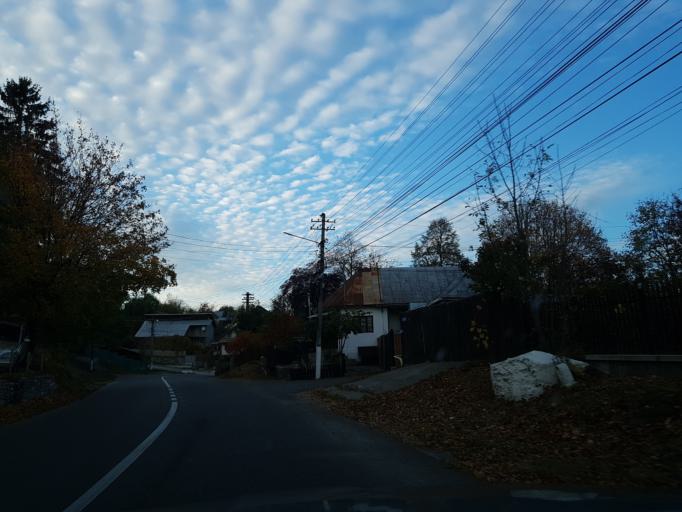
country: RO
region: Prahova
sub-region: Oras Breaza
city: Gura Beliei
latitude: 45.2038
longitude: 25.6495
